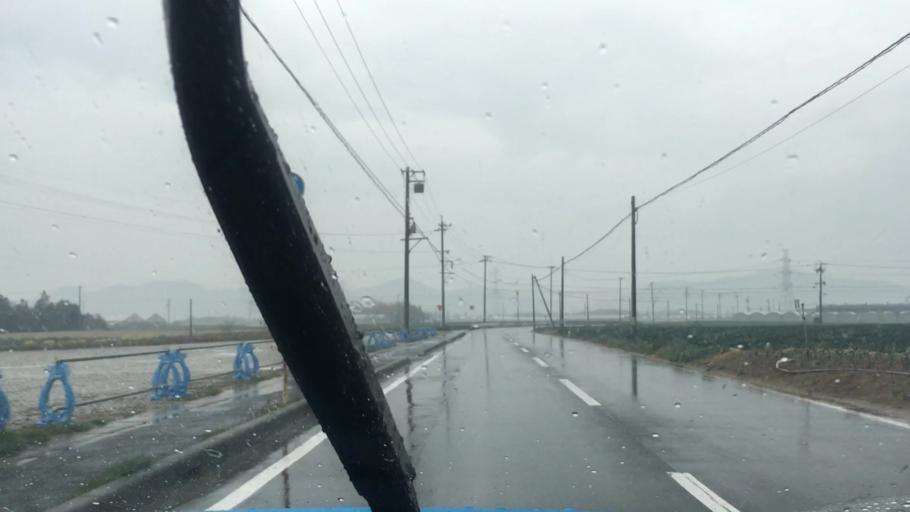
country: JP
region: Aichi
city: Tahara
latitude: 34.6485
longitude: 137.2938
